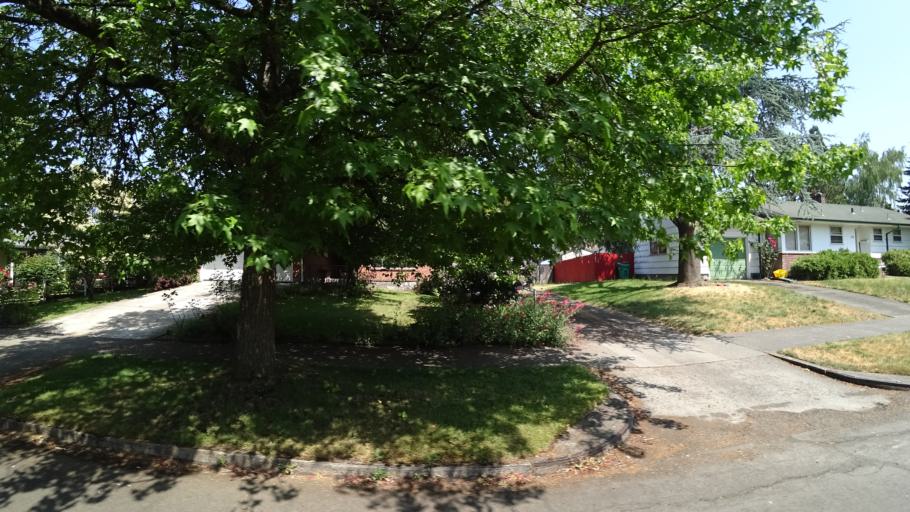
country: US
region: Oregon
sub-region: Multnomah County
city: Portland
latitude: 45.5796
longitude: -122.7054
